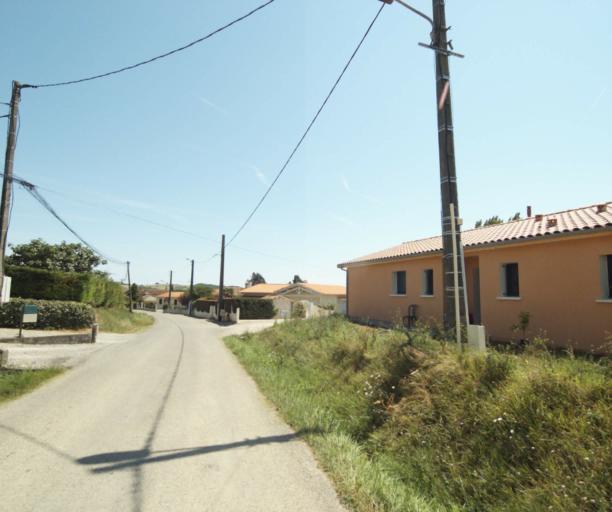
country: FR
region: Midi-Pyrenees
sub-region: Departement de l'Ariege
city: Lezat-sur-Leze
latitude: 43.2769
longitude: 1.3401
